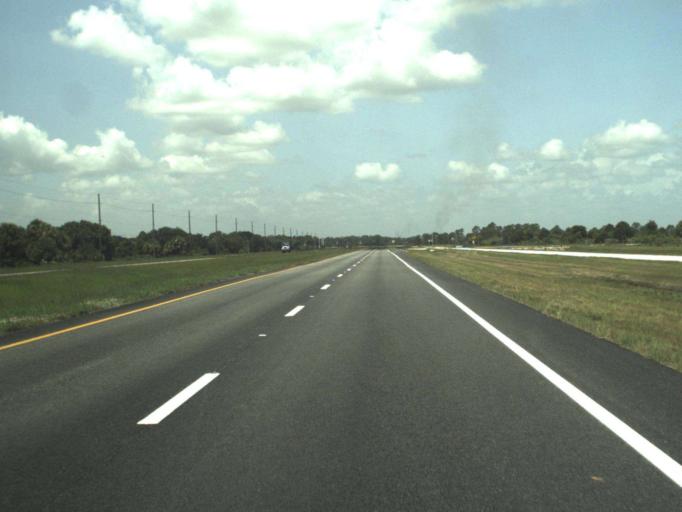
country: US
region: Florida
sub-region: Okeechobee County
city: Cypress Quarters
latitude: 27.3633
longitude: -80.6161
